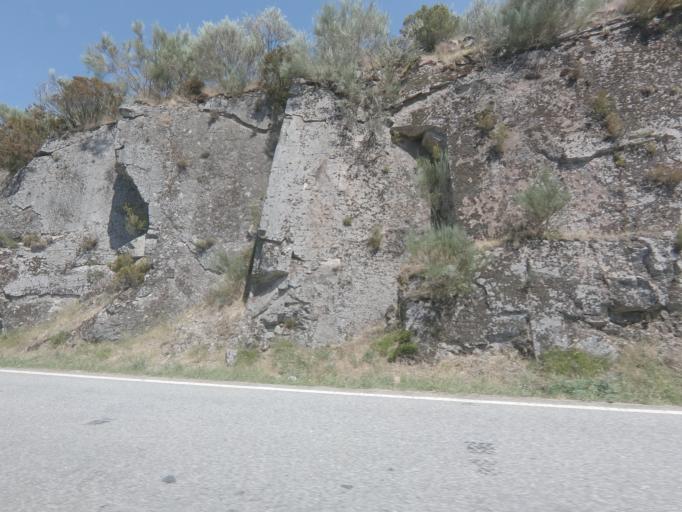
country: PT
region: Viseu
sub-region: Castro Daire
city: Castro Daire
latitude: 40.9887
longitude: -7.8847
